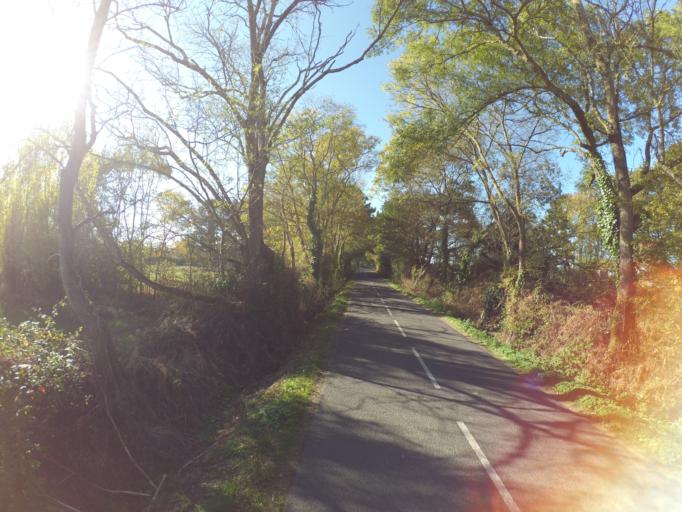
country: FR
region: Pays de la Loire
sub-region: Departement de la Loire-Atlantique
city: Saint-Lumine-de-Clisson
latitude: 47.0581
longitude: -1.3419
